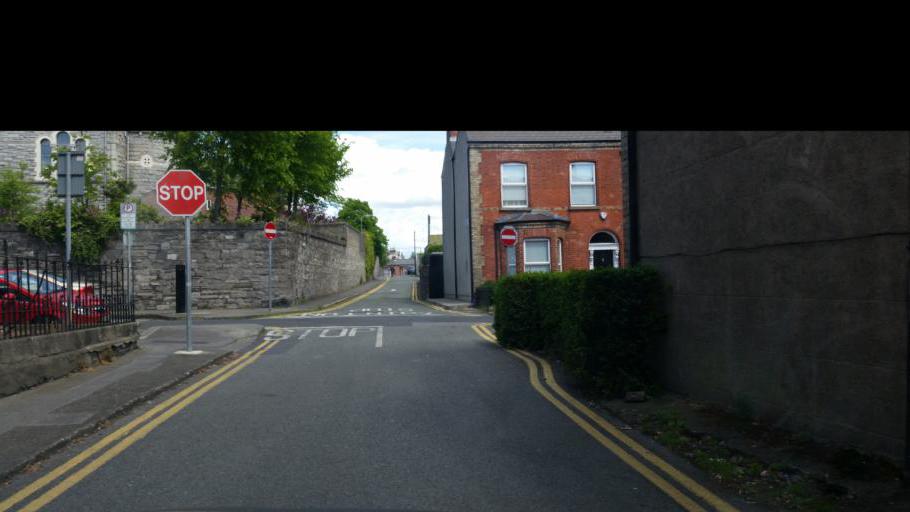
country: IE
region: Leinster
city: Drumcondra
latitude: 53.3645
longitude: -6.2590
